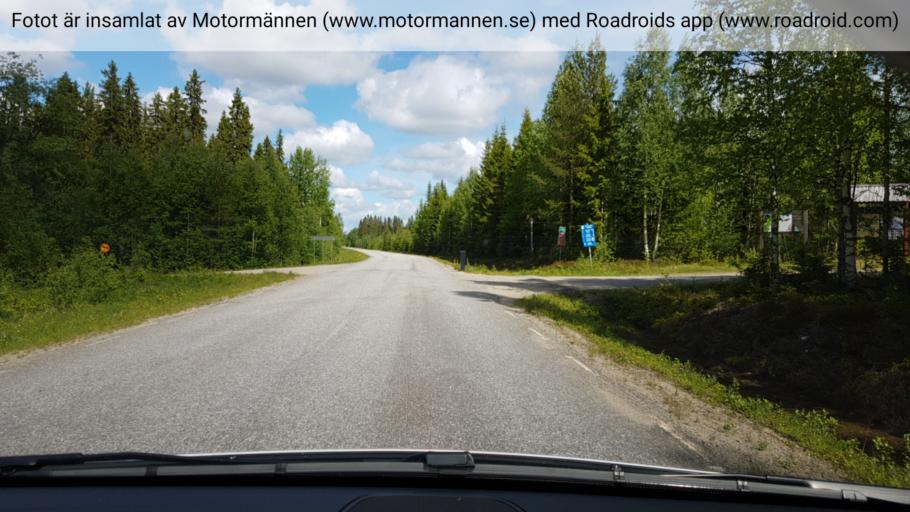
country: SE
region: Vaesterbotten
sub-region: Vannas Kommun
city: Vannasby
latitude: 64.0165
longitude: 19.9302
